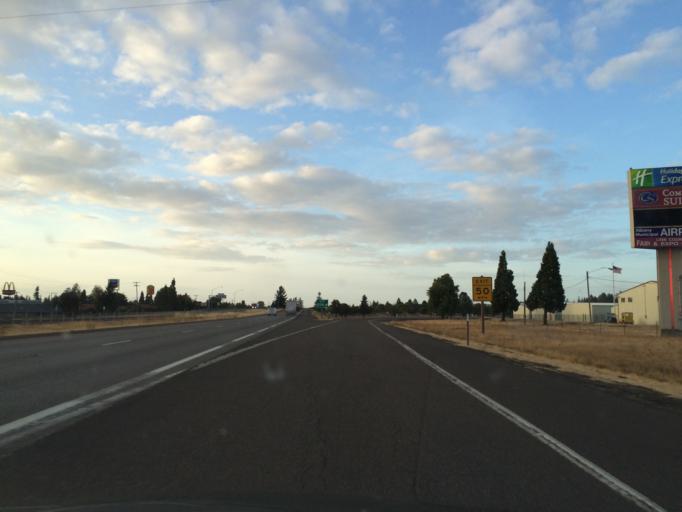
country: US
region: Oregon
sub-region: Linn County
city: Millersburg
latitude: 44.6393
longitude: -123.0622
